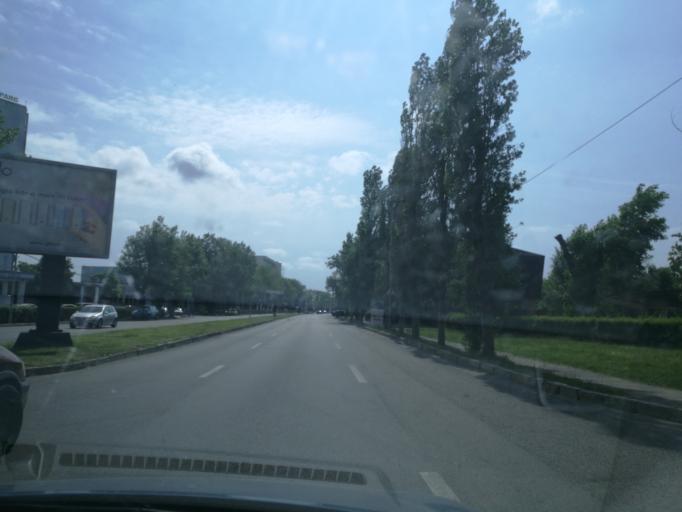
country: RO
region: Constanta
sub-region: Municipiul Constanta
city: Palazu Mare
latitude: 44.2180
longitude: 28.6355
